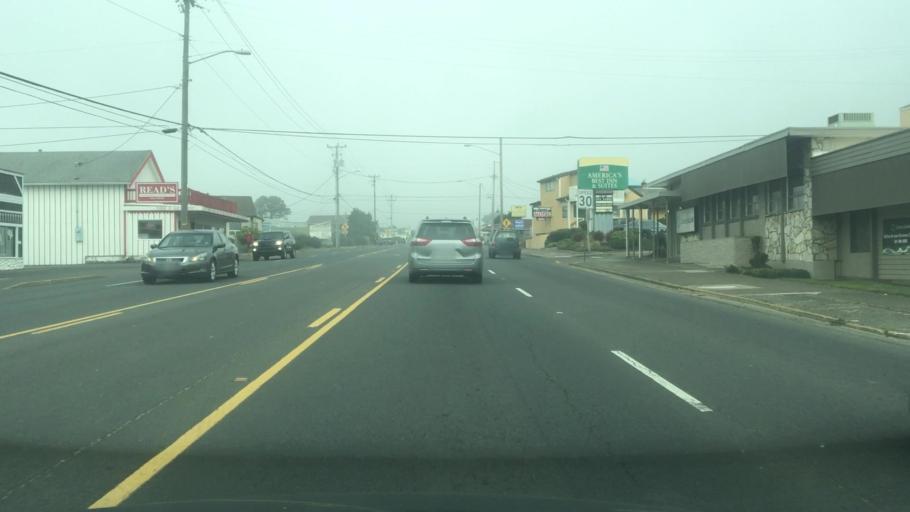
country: US
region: Oregon
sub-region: Lincoln County
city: Lincoln City
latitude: 44.9723
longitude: -124.0140
